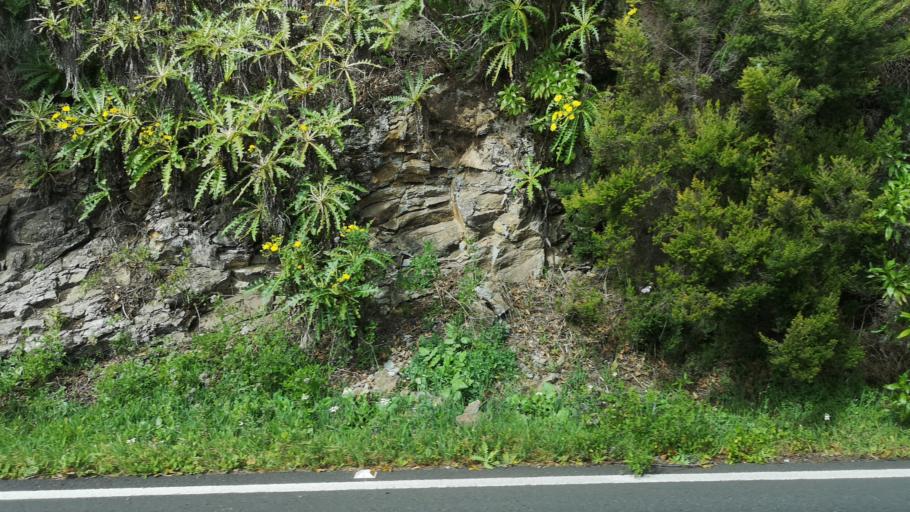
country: ES
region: Canary Islands
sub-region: Provincia de Santa Cruz de Tenerife
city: Alajero
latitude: 28.1082
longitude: -17.2301
